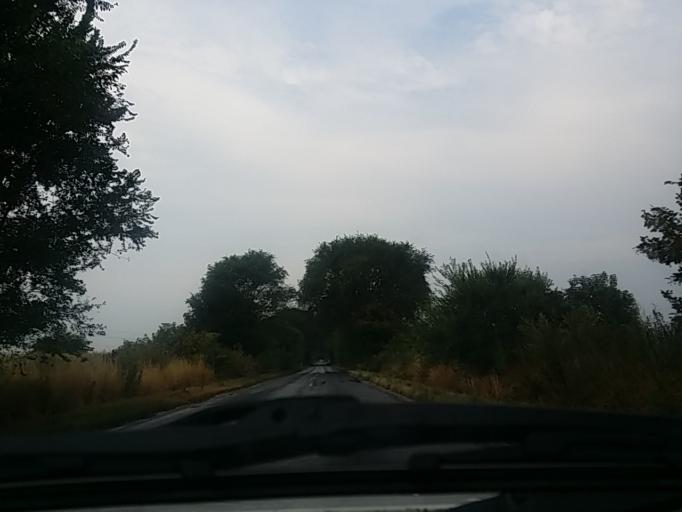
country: HU
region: Pest
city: Paty
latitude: 47.5316
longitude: 18.7833
